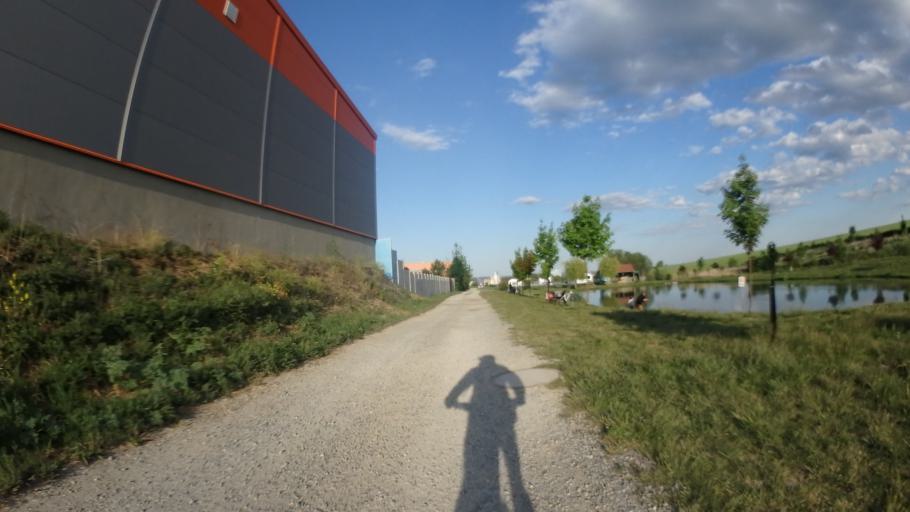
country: CZ
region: South Moravian
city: Moravany
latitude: 49.1436
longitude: 16.5902
